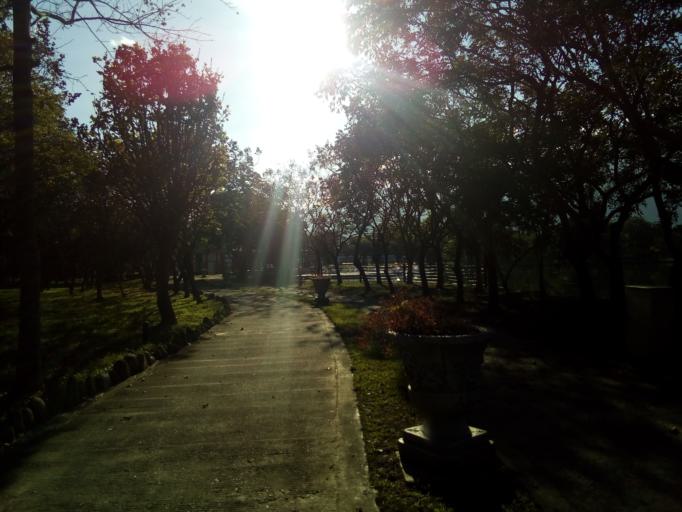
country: TW
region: Taiwan
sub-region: Taitung
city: Taitung
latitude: 23.0368
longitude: 121.1729
